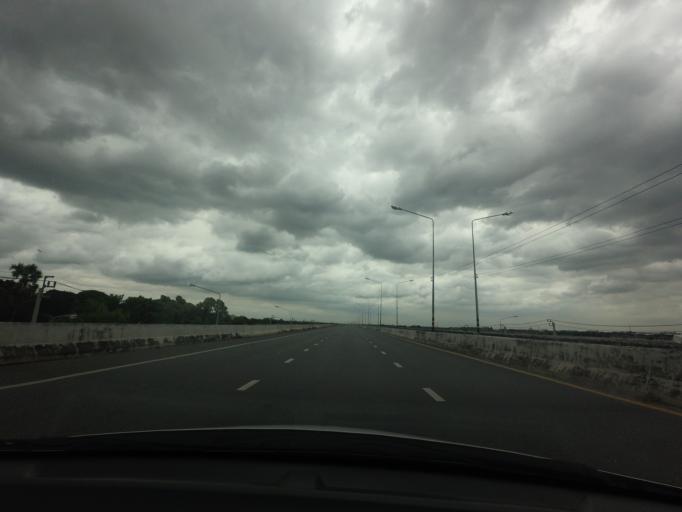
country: TH
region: Bangkok
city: Saphan Sung
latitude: 13.7547
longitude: 100.7236
